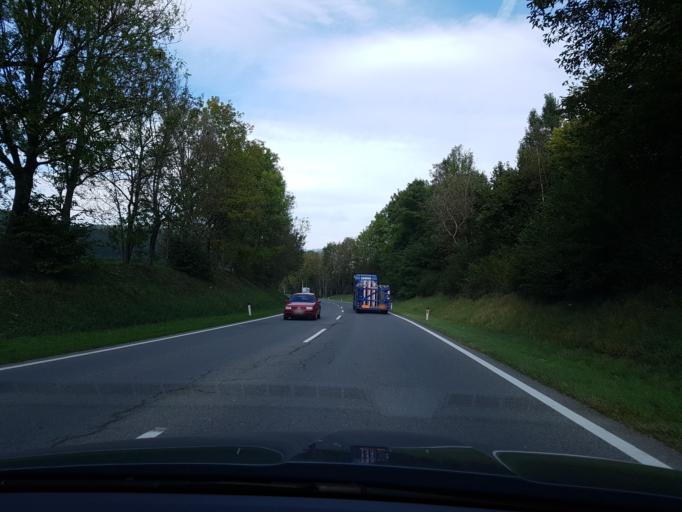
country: AT
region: Carinthia
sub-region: Politischer Bezirk Feldkirchen
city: Feldkirchen in Karnten
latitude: 46.7295
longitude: 14.1012
